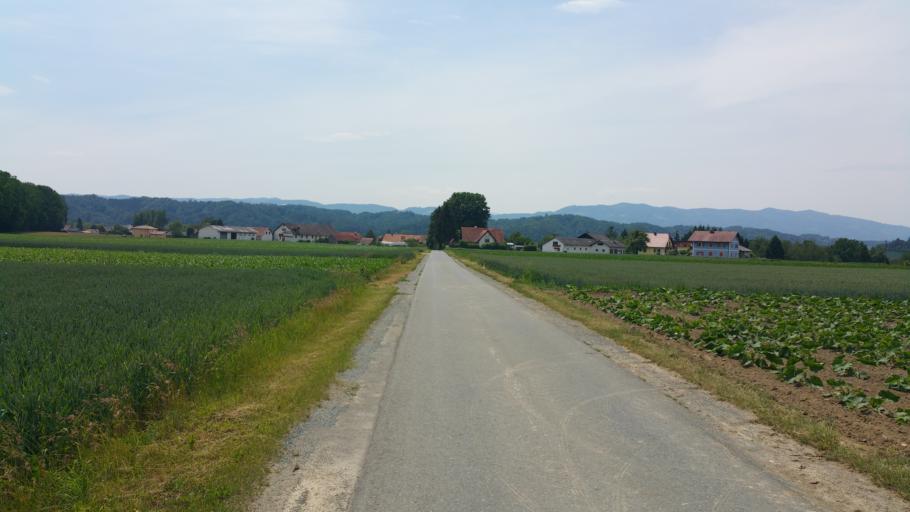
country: AT
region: Styria
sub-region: Politischer Bezirk Deutschlandsberg
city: Sankt Martin im Sulmtal
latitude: 46.7546
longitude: 15.3296
